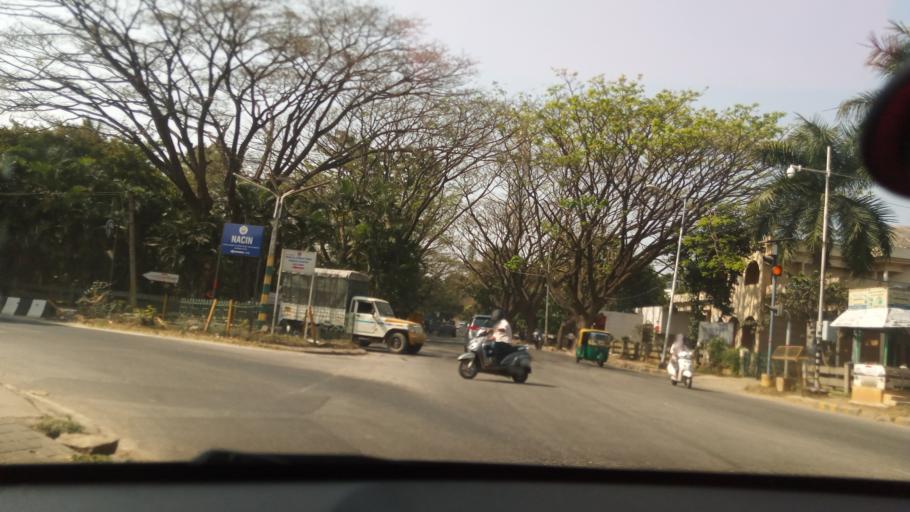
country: IN
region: Karnataka
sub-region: Bangalore Urban
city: Yelahanka
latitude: 13.0503
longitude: 77.5533
